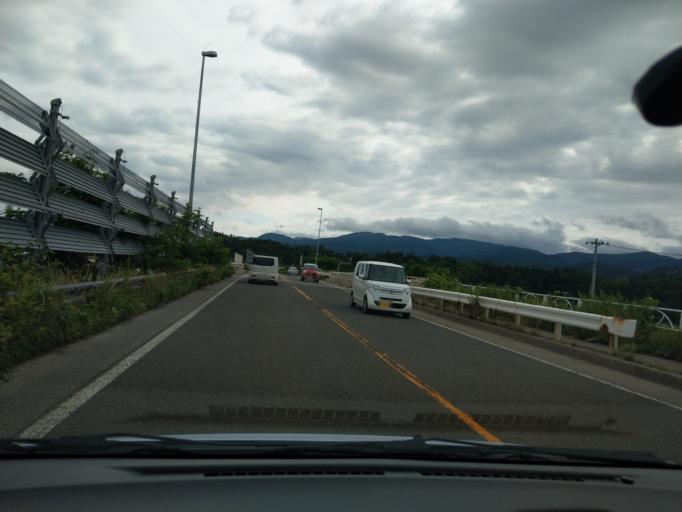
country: JP
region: Akita
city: Yokotemachi
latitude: 39.3301
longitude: 140.5568
